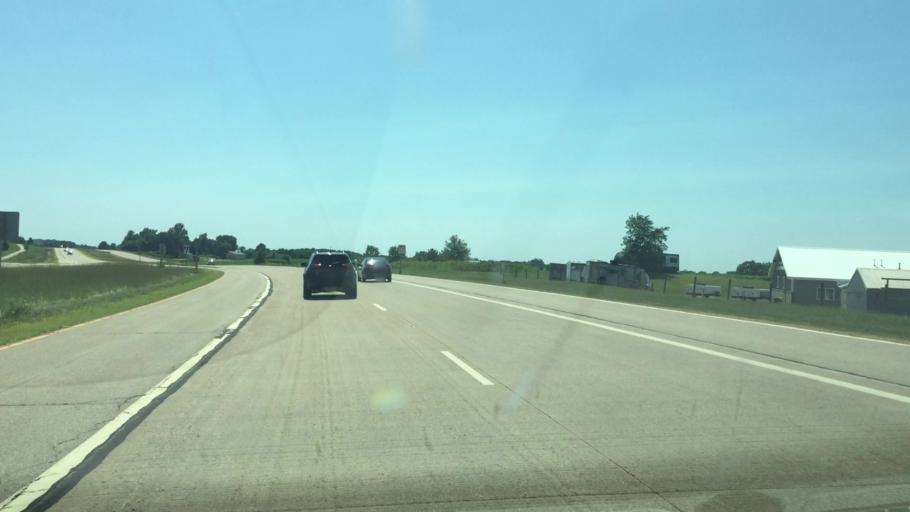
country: US
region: Wisconsin
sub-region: Grant County
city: Platteville
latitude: 42.7105
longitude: -90.5139
